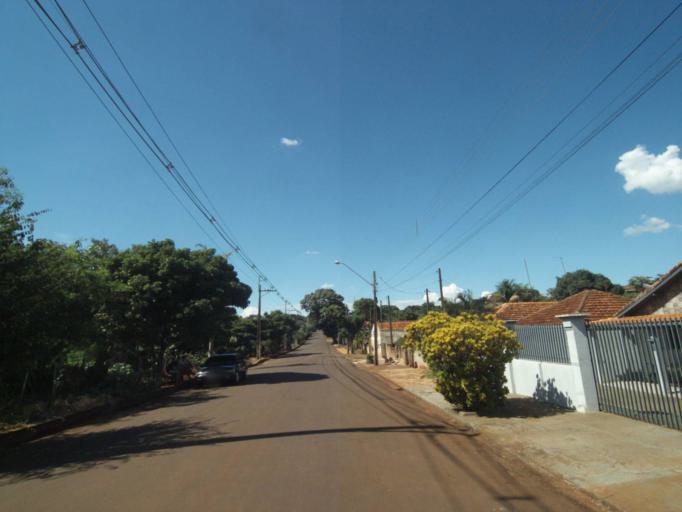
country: BR
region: Parana
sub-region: Sertanopolis
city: Sertanopolis
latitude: -23.0393
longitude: -50.8215
